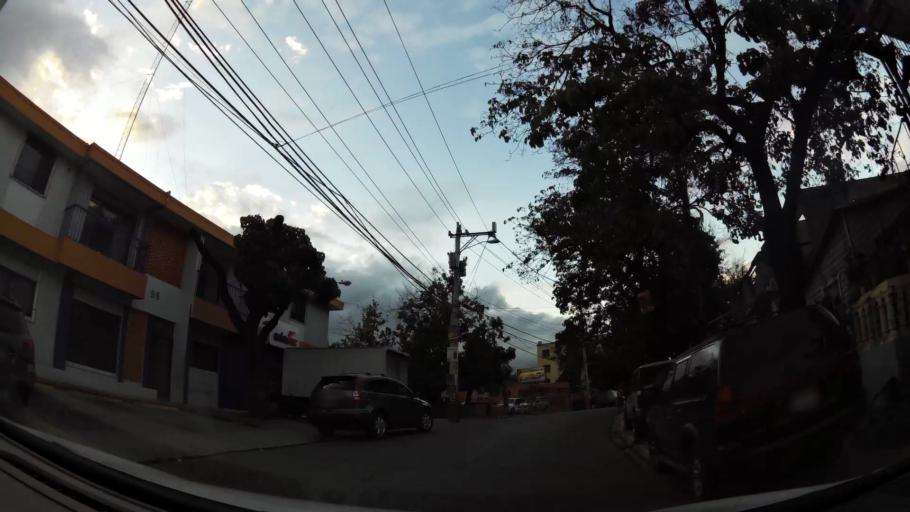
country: DO
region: Santo Domingo
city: Santo Domingo Oeste
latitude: 18.5238
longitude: -70.0150
